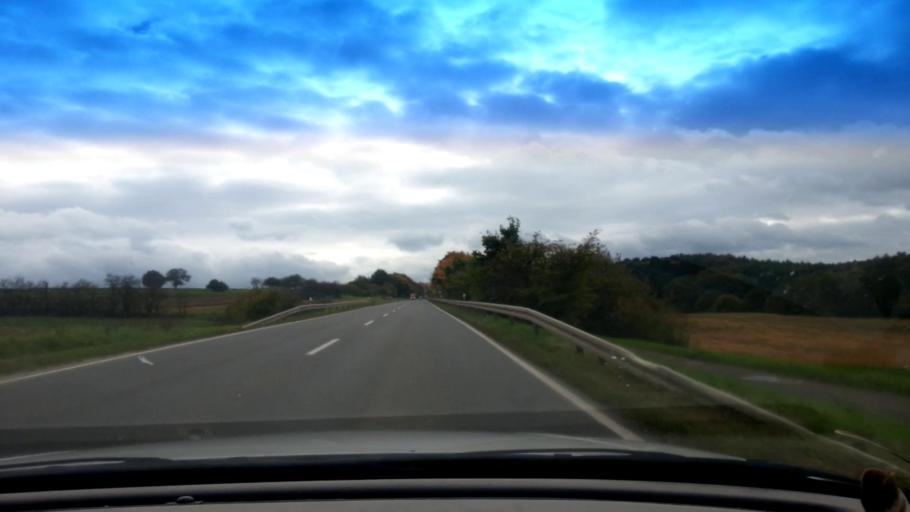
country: DE
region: Bavaria
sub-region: Upper Franconia
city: Viereth-Trunstadt
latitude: 49.9086
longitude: 10.7995
